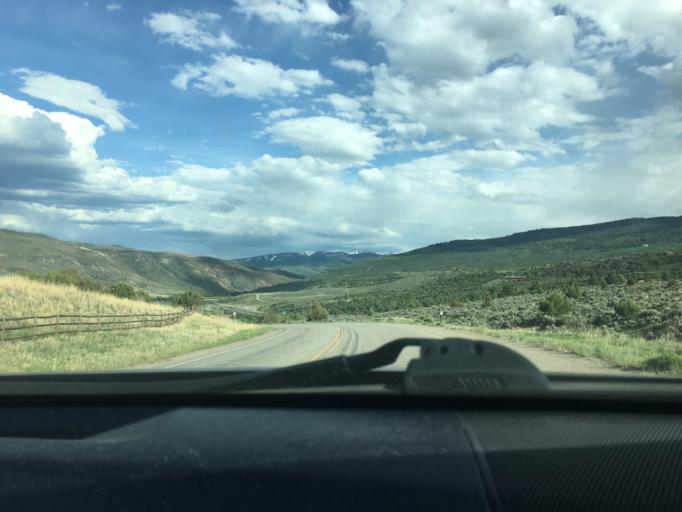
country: US
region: Colorado
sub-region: Eagle County
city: Edwards
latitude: 39.7066
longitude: -106.6854
